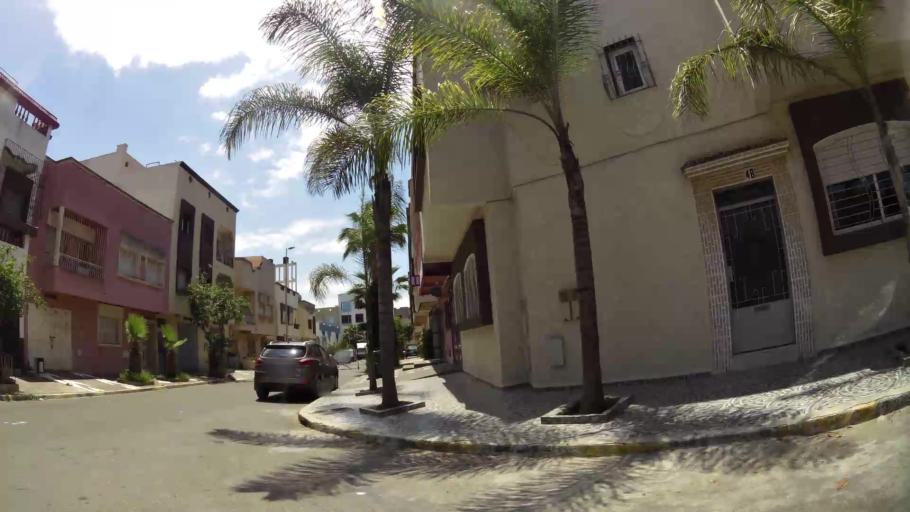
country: MA
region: Gharb-Chrarda-Beni Hssen
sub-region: Kenitra Province
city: Kenitra
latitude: 34.2689
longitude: -6.6168
